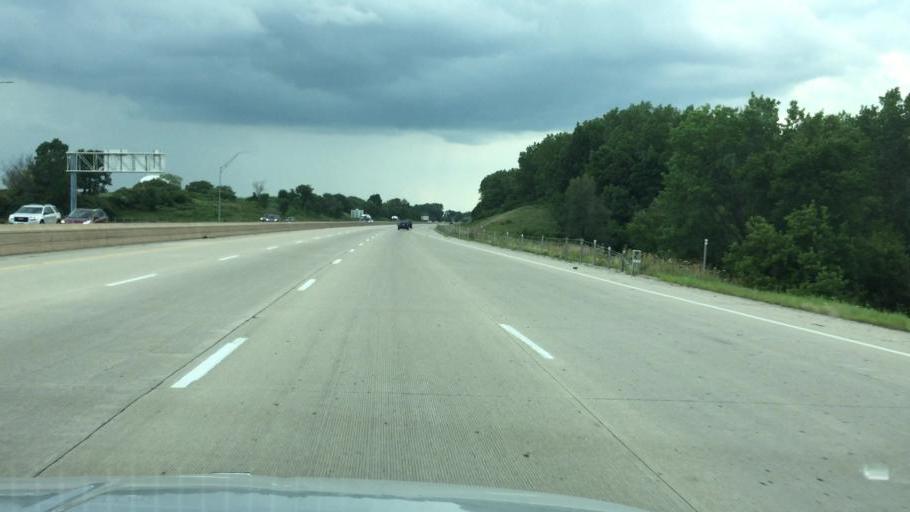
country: US
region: Iowa
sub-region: Johnson County
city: Coralville
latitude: 41.6862
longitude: -91.5688
